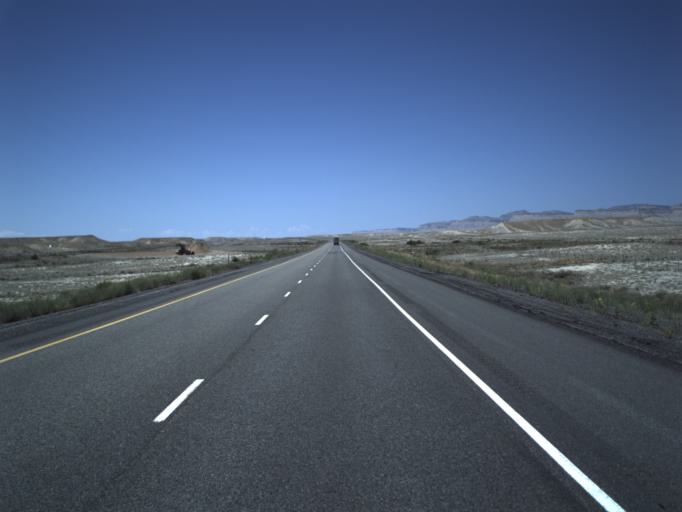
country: US
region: Utah
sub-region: Grand County
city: Moab
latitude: 38.9402
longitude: -109.5042
